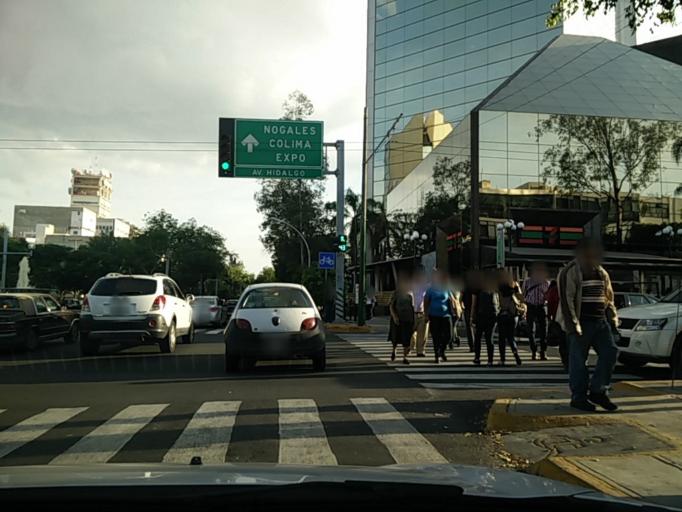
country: MX
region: Jalisco
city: Guadalajara
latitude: 20.6770
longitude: -103.3690
